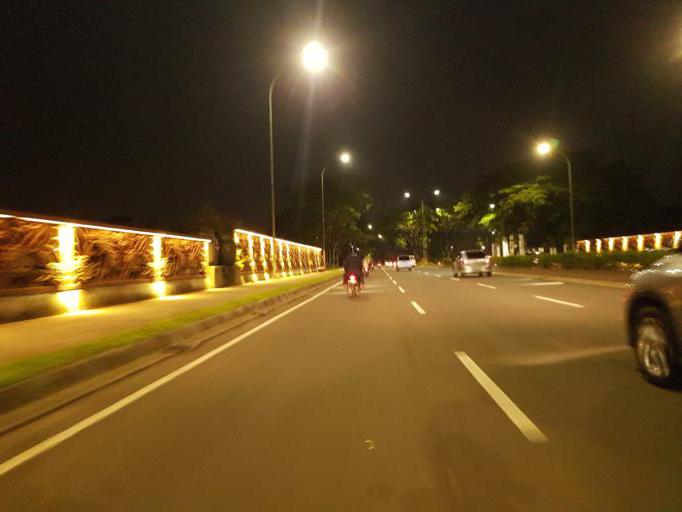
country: ID
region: West Java
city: Serpong
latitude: -6.2988
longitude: 106.6538
